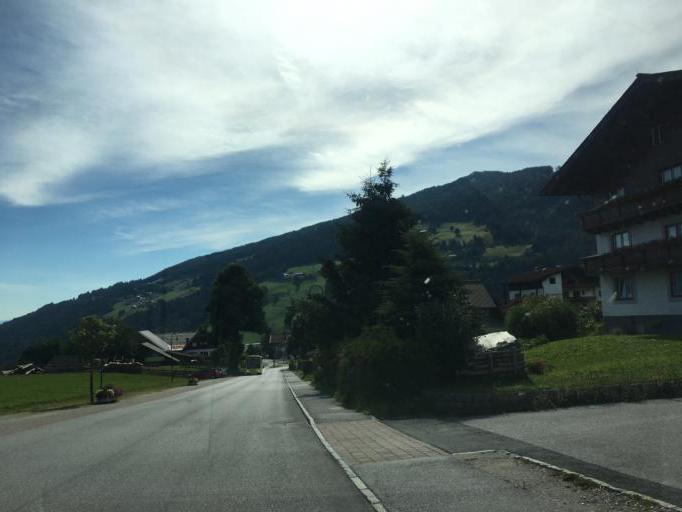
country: AT
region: Styria
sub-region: Politischer Bezirk Liezen
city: Schladming
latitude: 47.3834
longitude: 13.6704
